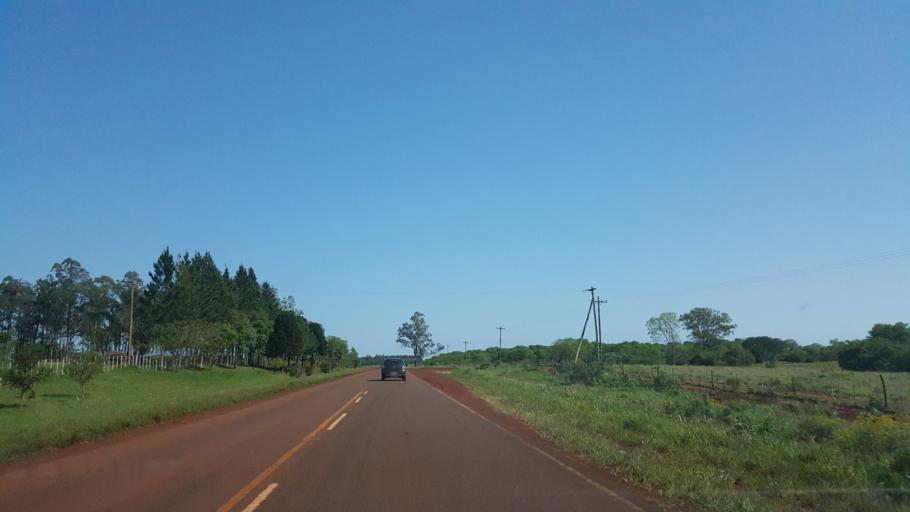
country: AR
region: Misiones
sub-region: Departamento de Apostoles
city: San Jose
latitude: -27.7810
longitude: -55.8398
